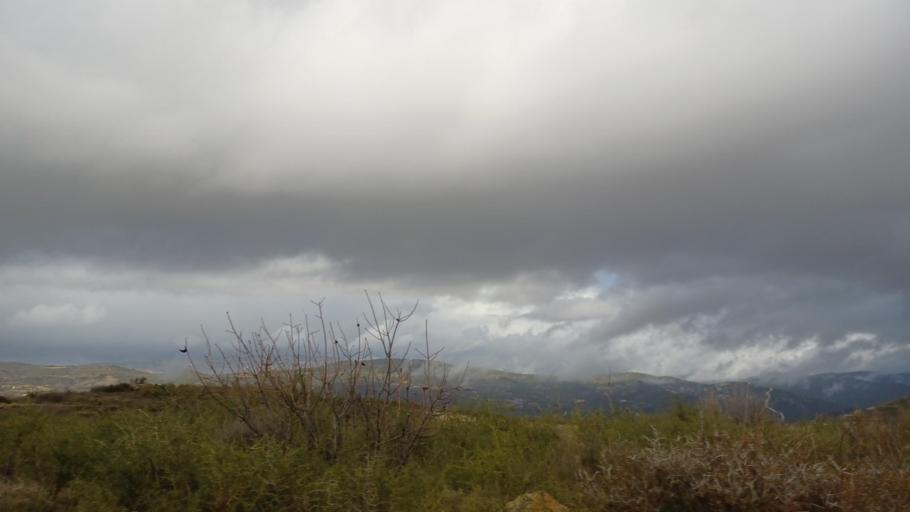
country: CY
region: Limassol
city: Pachna
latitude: 34.8297
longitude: 32.7438
